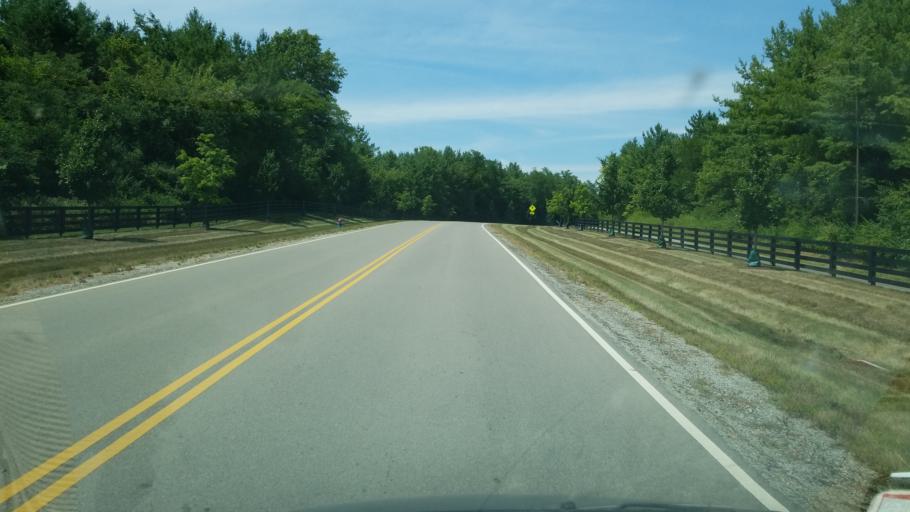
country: US
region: Ohio
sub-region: Union County
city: New California
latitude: 40.1762
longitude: -83.1889
